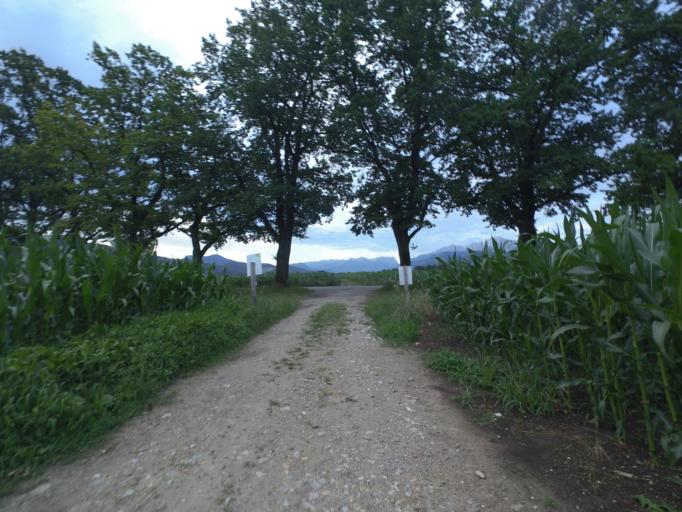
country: AT
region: Salzburg
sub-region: Politischer Bezirk Salzburg-Umgebung
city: Anif
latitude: 47.7605
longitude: 13.0522
